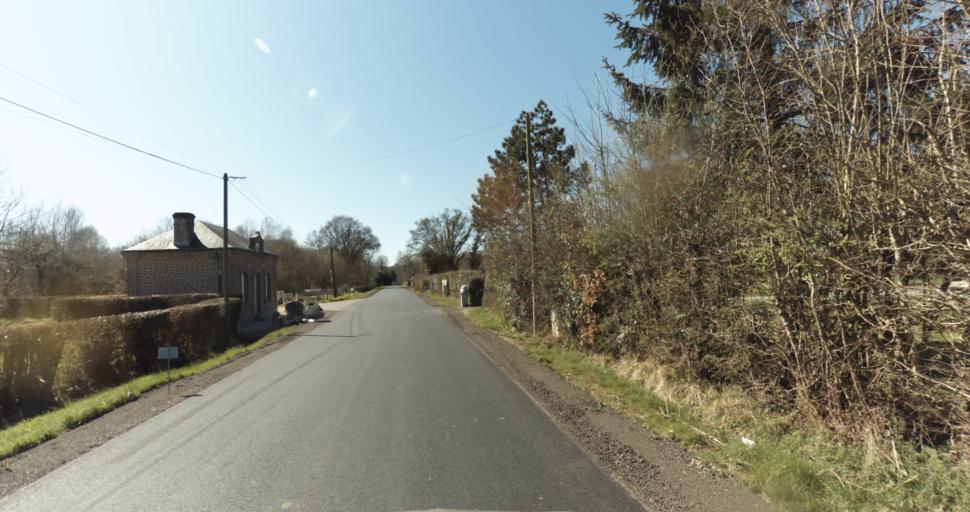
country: FR
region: Lower Normandy
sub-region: Departement du Calvados
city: Livarot
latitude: 48.9404
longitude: 0.0825
